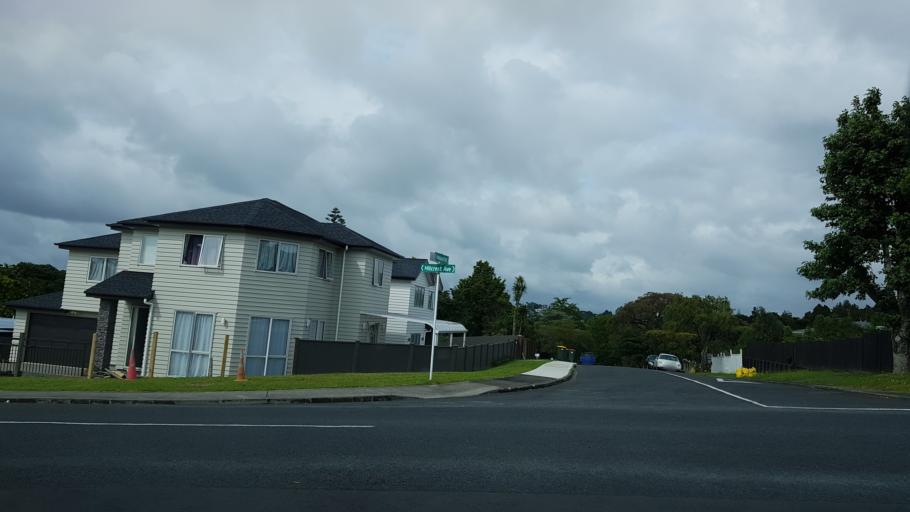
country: NZ
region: Auckland
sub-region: Auckland
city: North Shore
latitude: -36.7904
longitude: 174.7393
